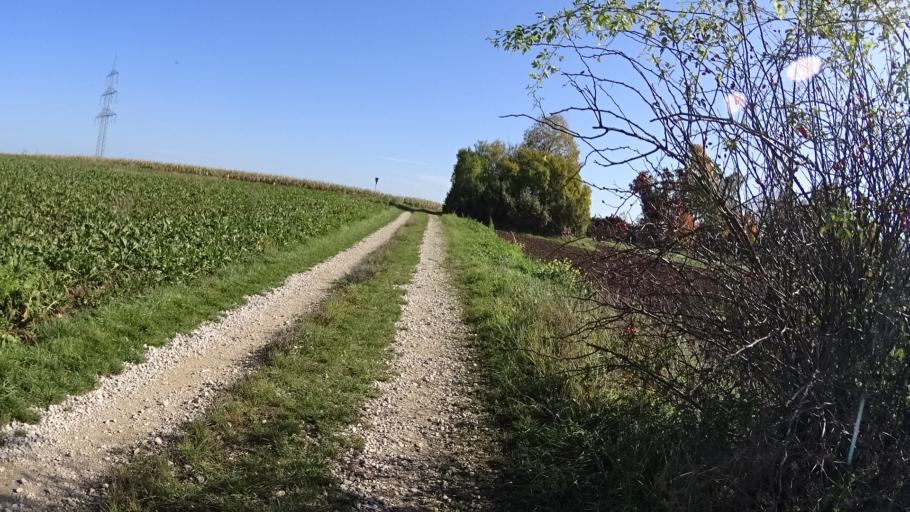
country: DE
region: Bavaria
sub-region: Upper Bavaria
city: Hitzhofen
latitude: 48.8644
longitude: 11.3323
